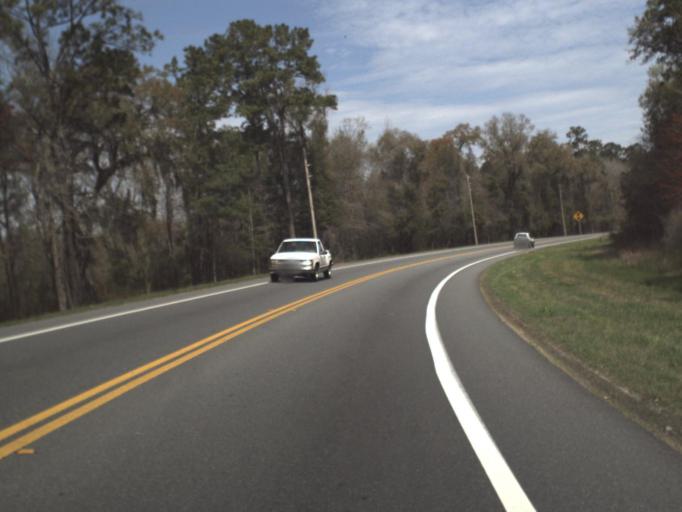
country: US
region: Florida
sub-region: Gadsden County
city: Midway
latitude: 30.4881
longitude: -84.3632
